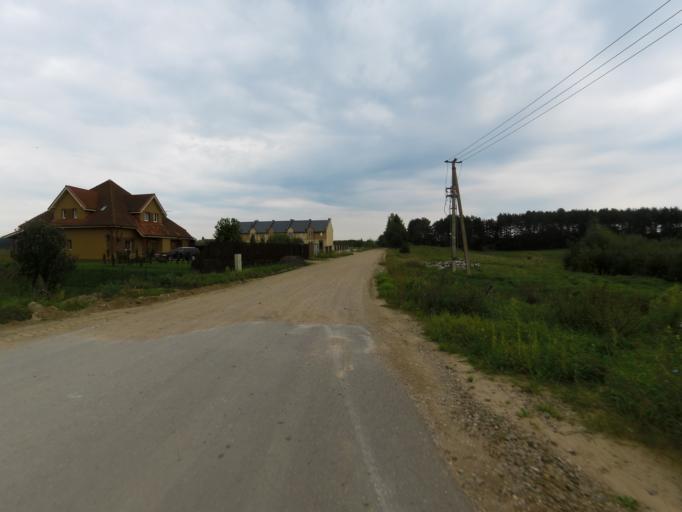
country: LT
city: Grigiskes
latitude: 54.7076
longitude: 25.1274
